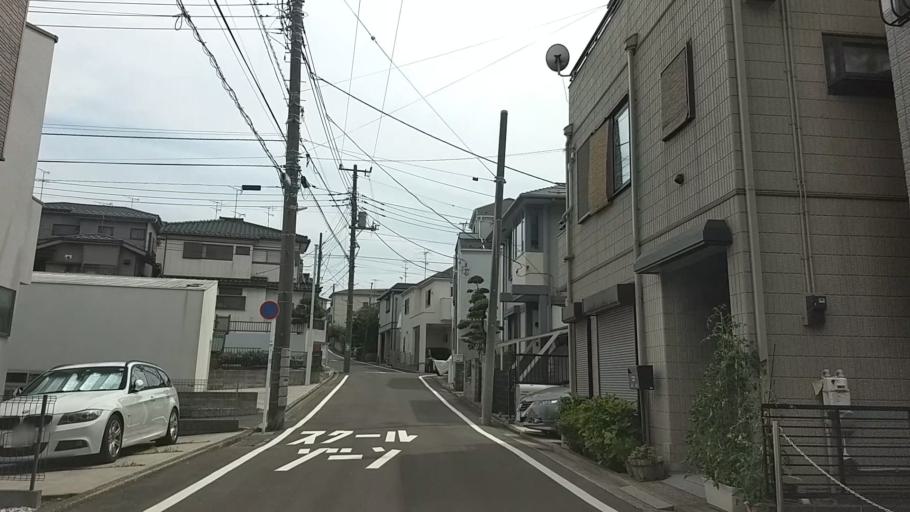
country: JP
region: Kanagawa
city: Yokohama
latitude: 35.4413
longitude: 139.6013
